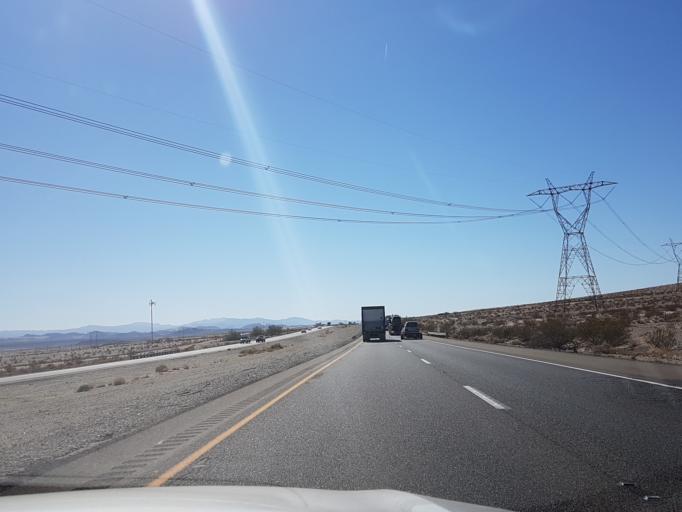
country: US
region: California
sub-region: San Bernardino County
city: Fort Irwin
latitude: 35.0507
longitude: -116.4436
